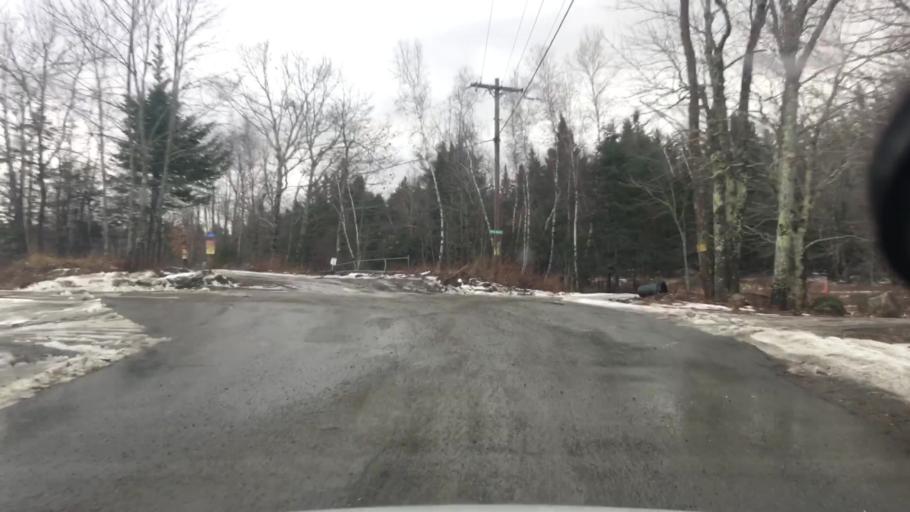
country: US
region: Maine
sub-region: Penobscot County
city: Orrington
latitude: 44.6794
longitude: -68.7560
